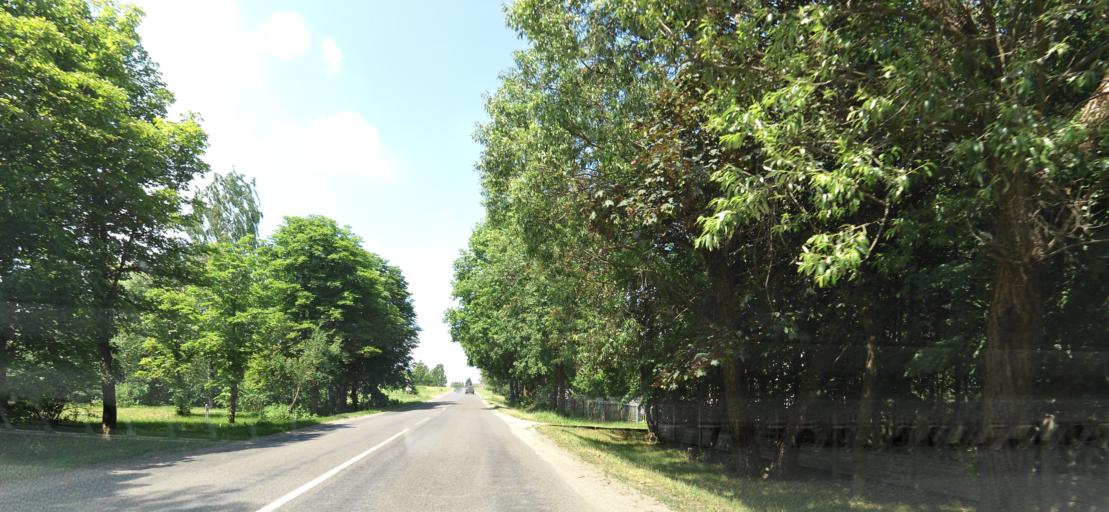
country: LT
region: Vilnius County
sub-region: Vilnius
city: Fabijoniskes
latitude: 54.8046
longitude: 25.2691
